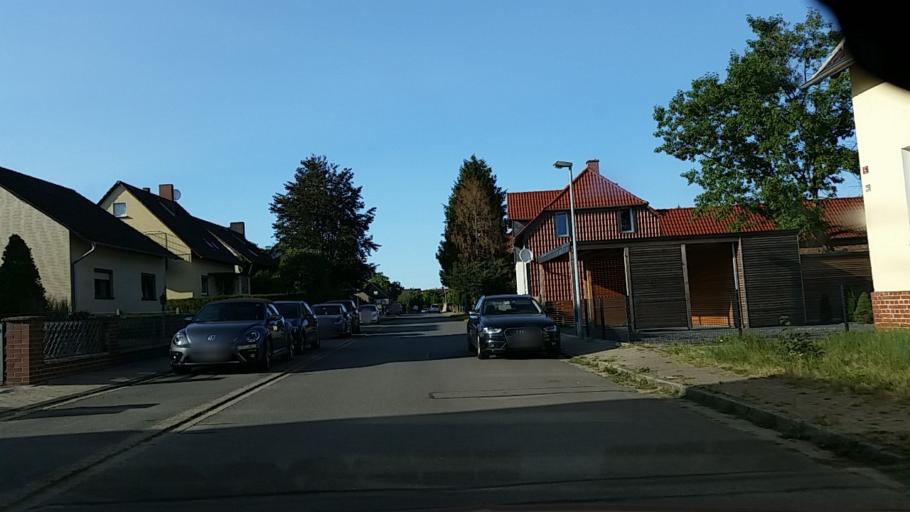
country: DE
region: Lower Saxony
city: Lehre
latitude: 52.3941
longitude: 10.6926
